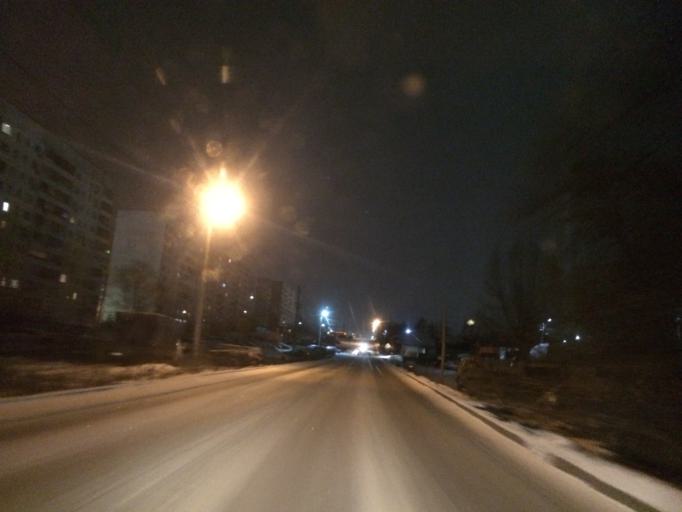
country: RU
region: Tula
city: Tula
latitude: 54.2071
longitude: 37.6426
